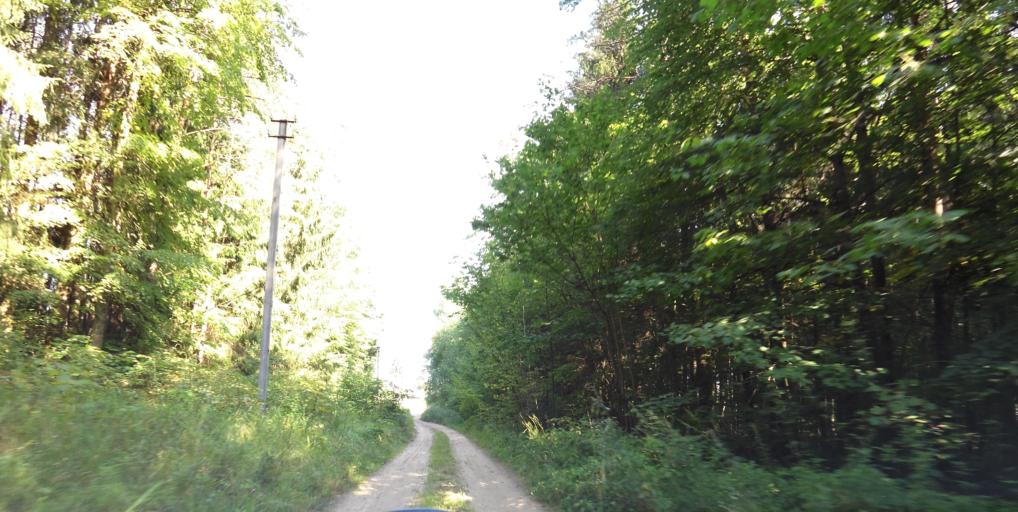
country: LT
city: Grigiskes
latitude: 54.7468
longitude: 25.0226
